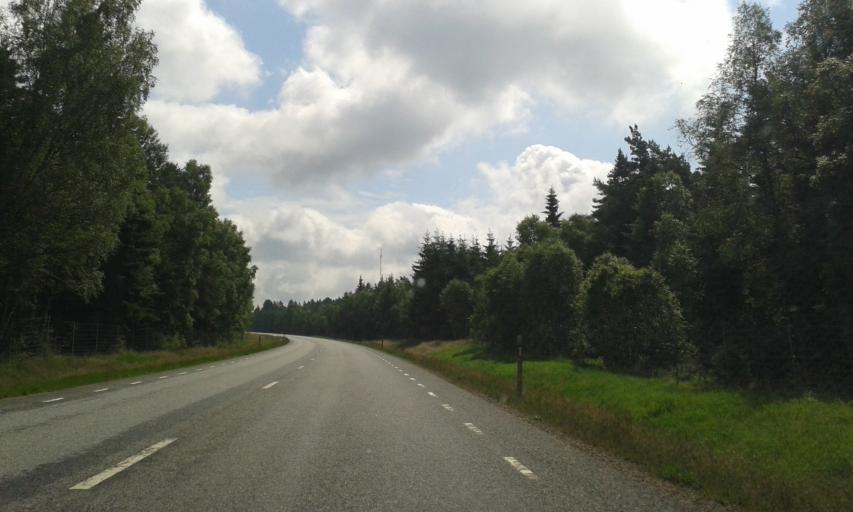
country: SE
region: Vaestra Goetaland
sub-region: Tranemo Kommun
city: Langhem
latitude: 57.5688
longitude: 13.2424
